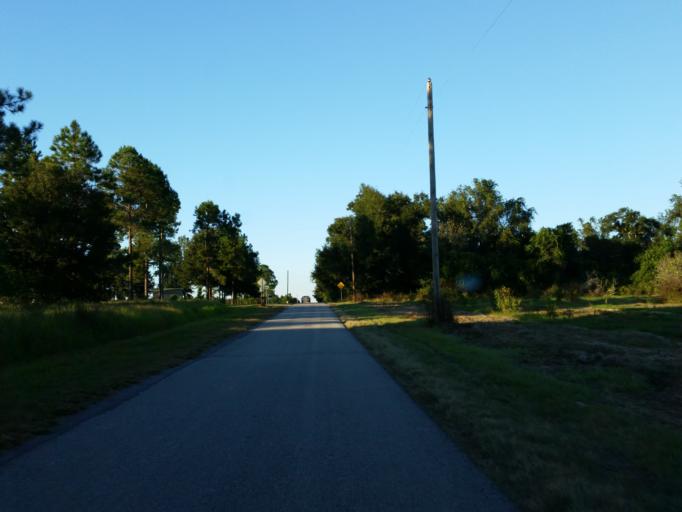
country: US
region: Florida
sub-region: Pasco County
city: Dade City North
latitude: 28.4282
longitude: -82.2698
